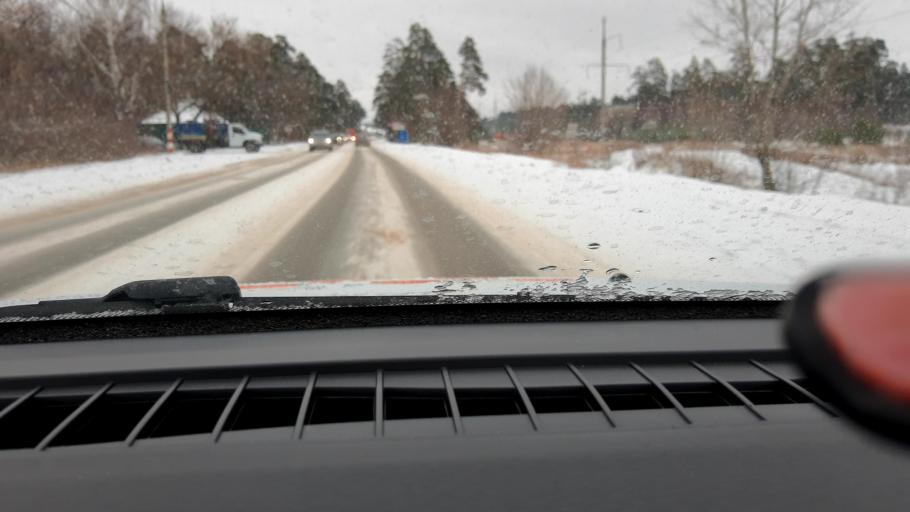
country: RU
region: Nizjnij Novgorod
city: Bor
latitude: 56.3301
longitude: 44.1201
